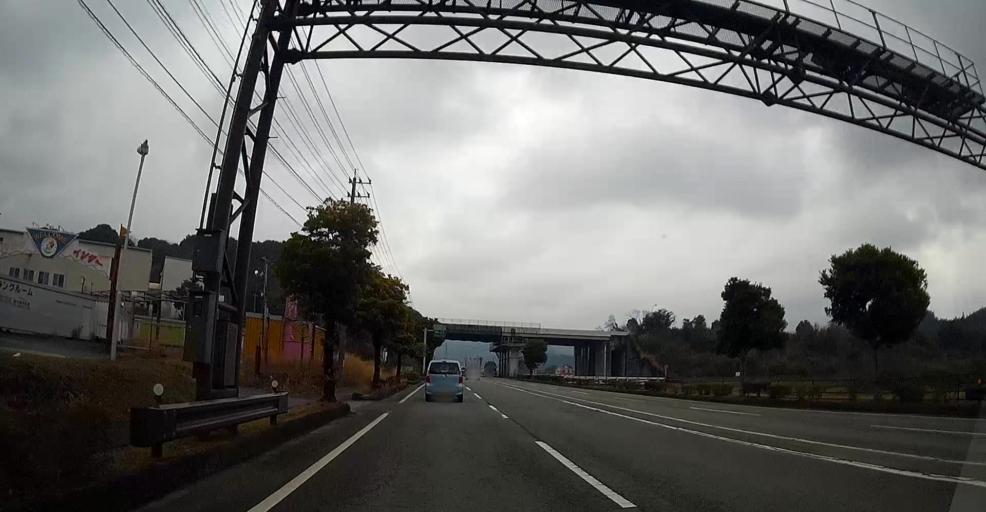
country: JP
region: Kumamoto
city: Matsubase
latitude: 32.6509
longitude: 130.7083
